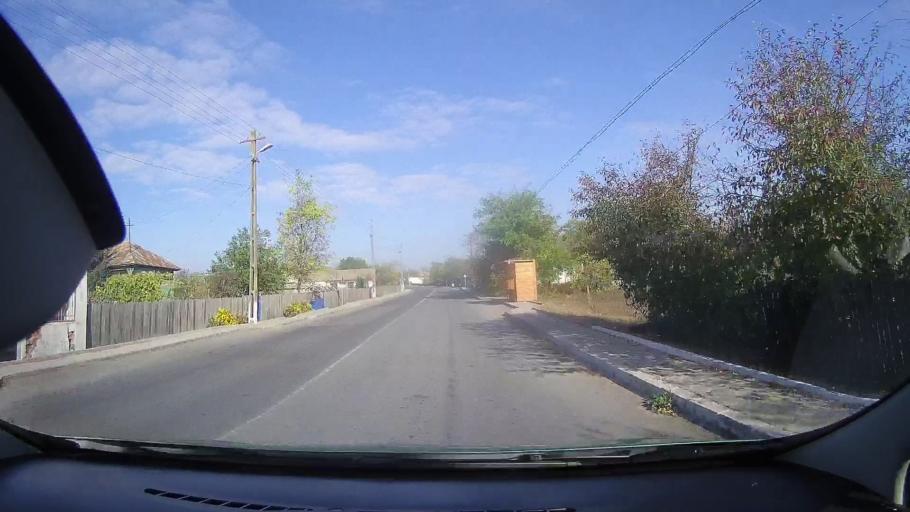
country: RO
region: Tulcea
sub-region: Comuna Valea Nucarilor
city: Iazurile
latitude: 45.0227
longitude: 28.9453
